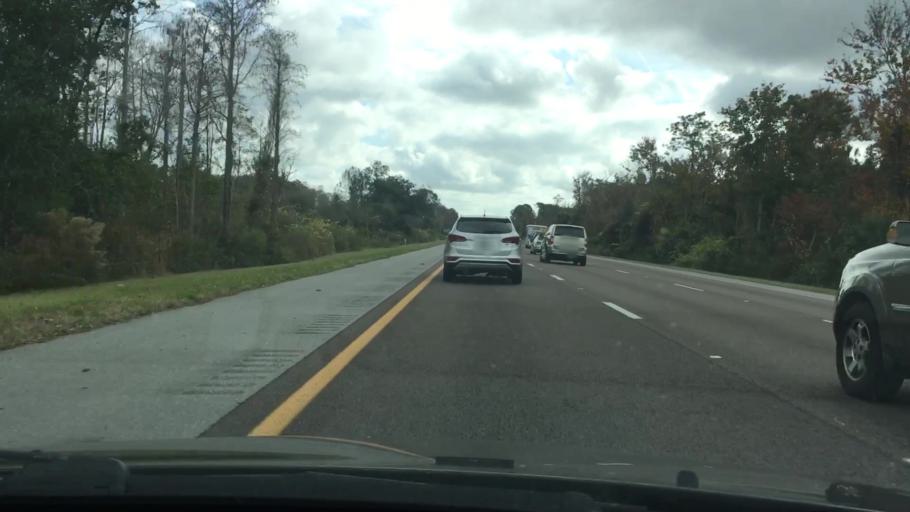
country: US
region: Florida
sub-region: Volusia County
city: Glencoe
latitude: 28.9760
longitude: -80.9641
